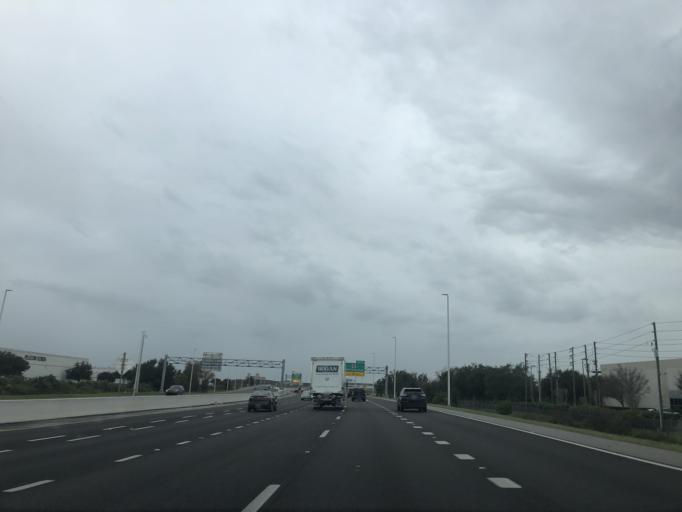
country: US
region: Florida
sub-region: Orange County
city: Williamsburg
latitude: 28.4296
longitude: -81.4168
